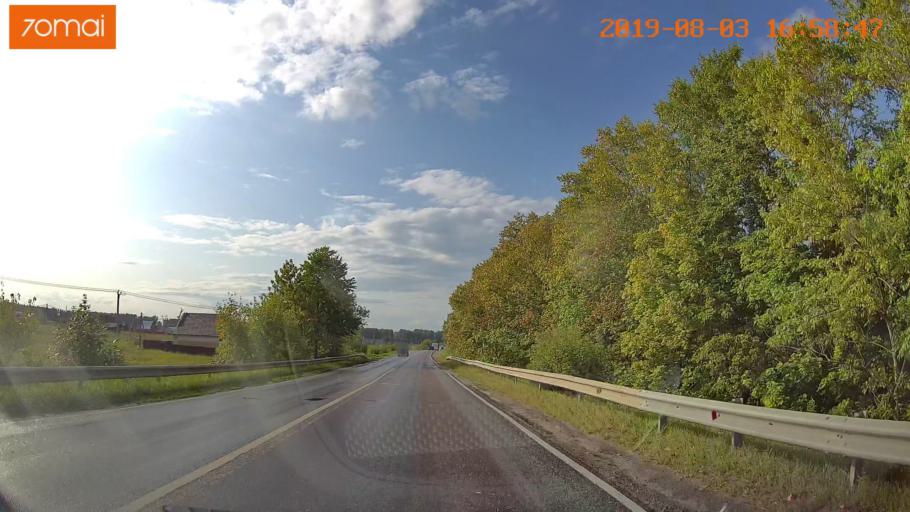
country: RU
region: Moskovskaya
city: Voskresensk
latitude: 55.3242
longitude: 38.6308
